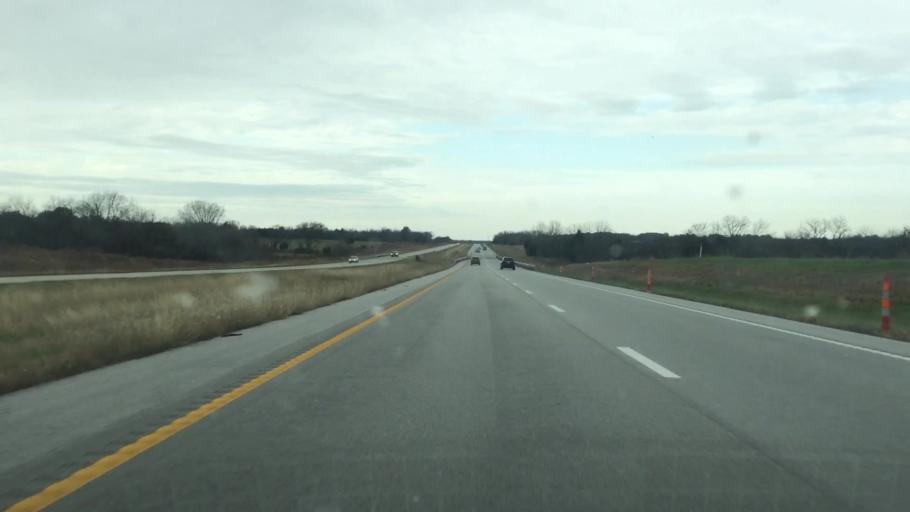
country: US
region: Missouri
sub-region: Saint Clair County
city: Osceola
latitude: 38.1932
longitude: -93.7422
